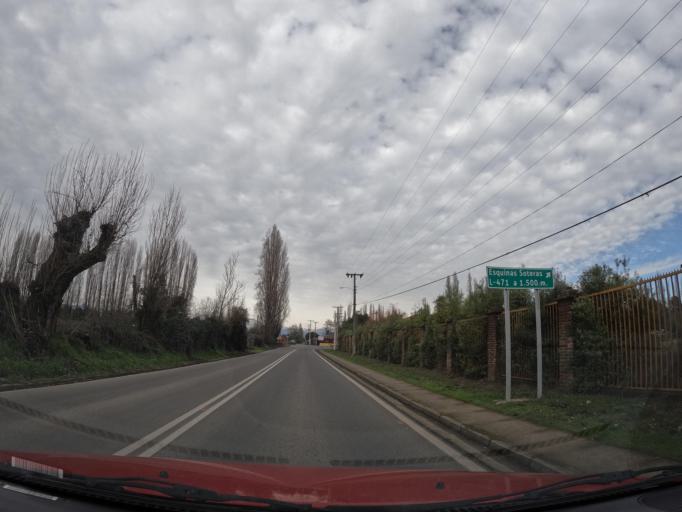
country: CL
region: Maule
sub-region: Provincia de Linares
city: Linares
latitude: -35.8754
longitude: -71.5418
